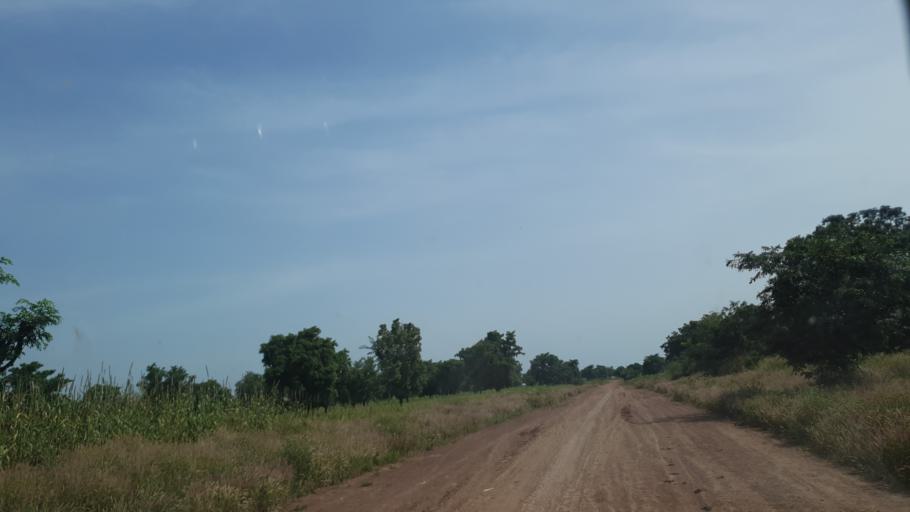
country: ML
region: Koulikoro
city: Dioila
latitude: 12.4219
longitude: -6.2276
